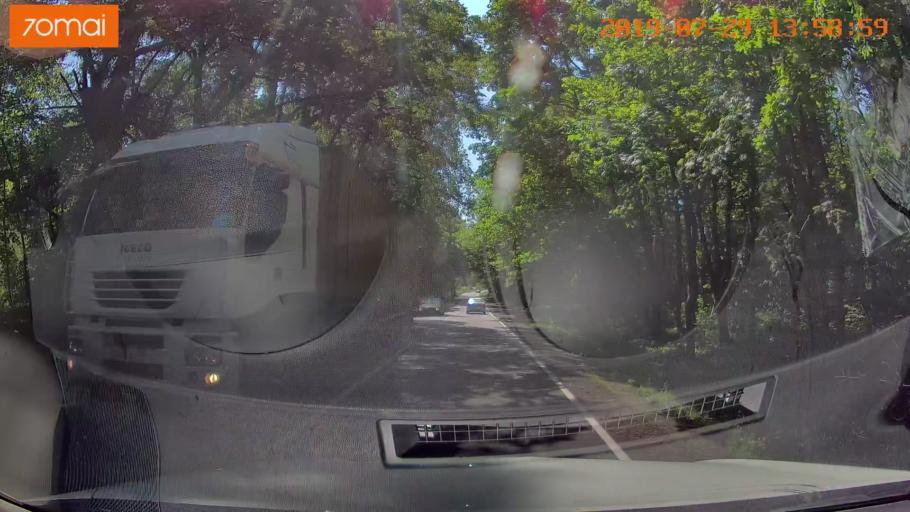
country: RU
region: Kaliningrad
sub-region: Gorod Kaliningrad
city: Baltiysk
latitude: 54.6885
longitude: 19.9348
